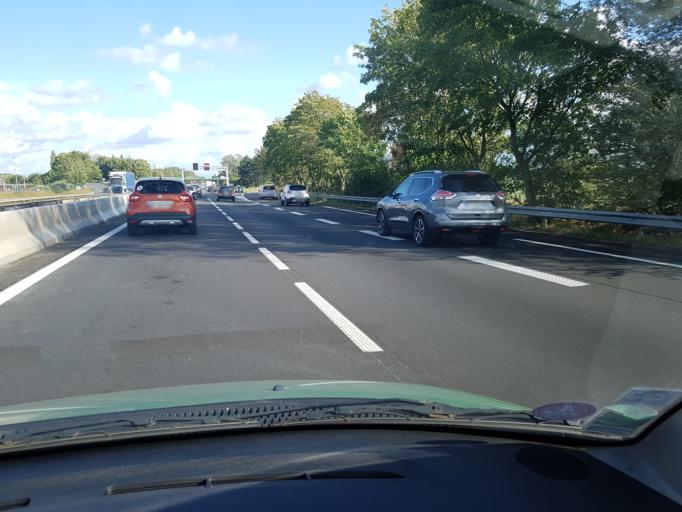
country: FR
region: Nord-Pas-de-Calais
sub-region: Departement du Nord
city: Erquinghem-Lys
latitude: 50.6853
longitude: 2.8368
